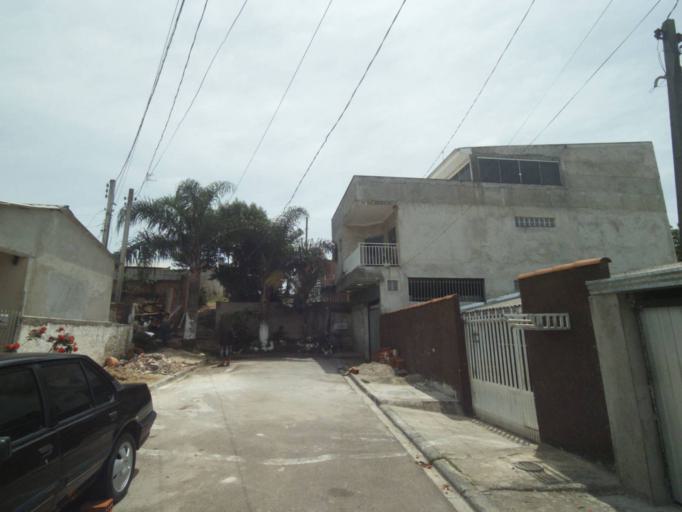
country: BR
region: Parana
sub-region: Curitiba
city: Curitiba
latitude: -25.5003
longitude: -49.3393
